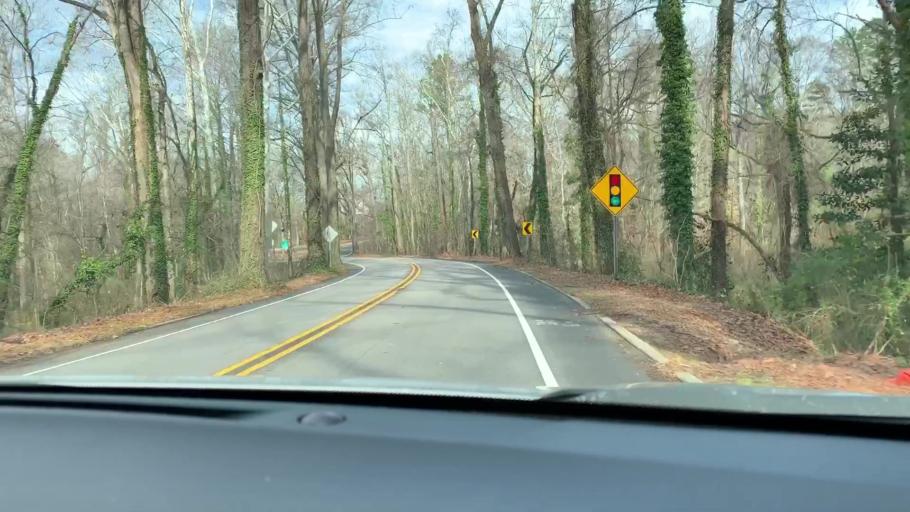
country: US
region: North Carolina
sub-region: Durham County
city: Durham
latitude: 35.9902
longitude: -78.9398
